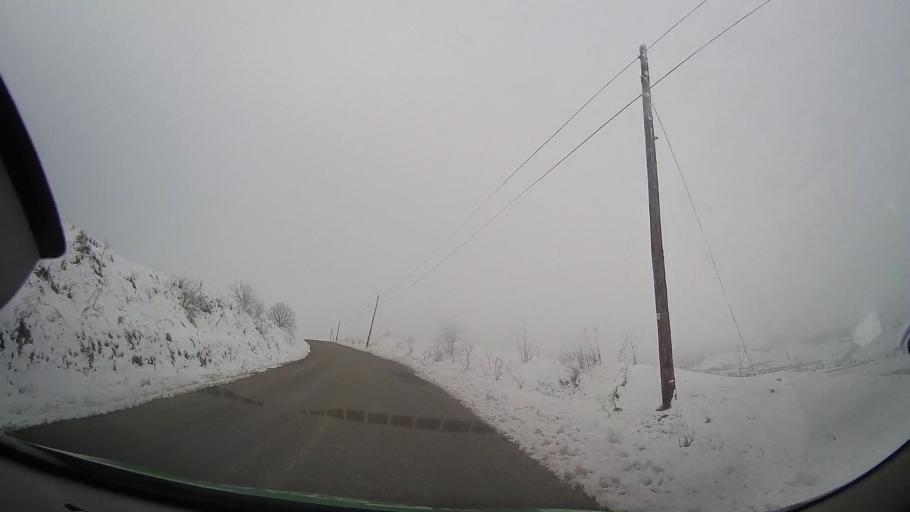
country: RO
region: Bacau
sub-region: Comuna Stanisesti
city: Stanisesti
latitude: 46.4115
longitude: 27.2701
